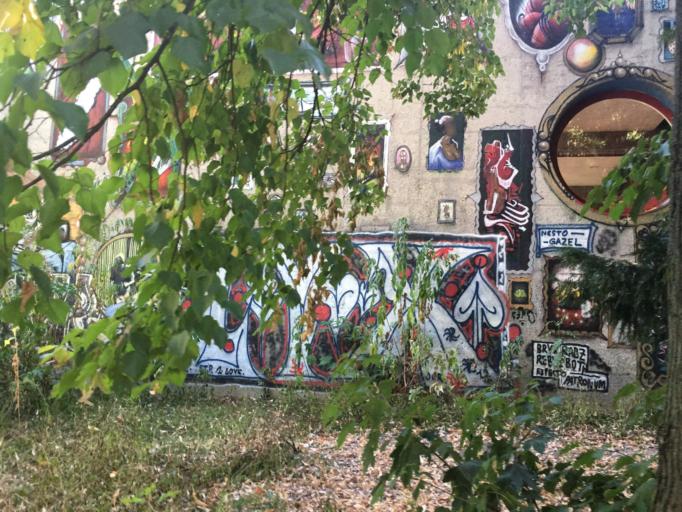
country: CH
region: Geneva
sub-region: Geneva
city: Geneve
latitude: 46.2126
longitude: 6.1361
